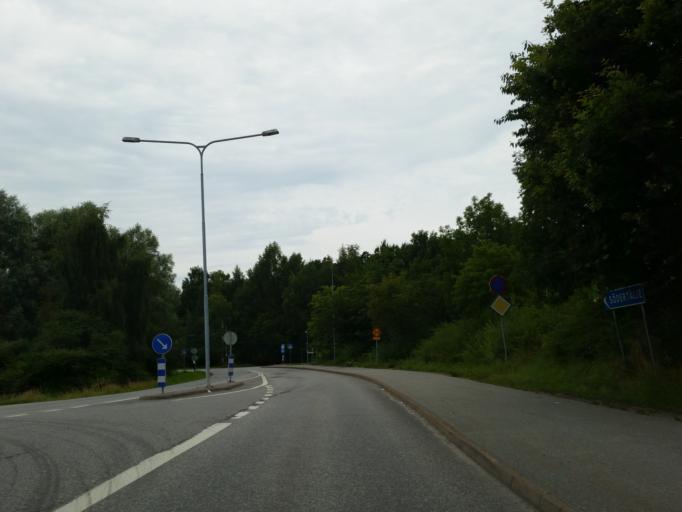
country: SE
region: Stockholm
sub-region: Botkyrka Kommun
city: Eriksberg
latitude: 59.2406
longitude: 17.8292
